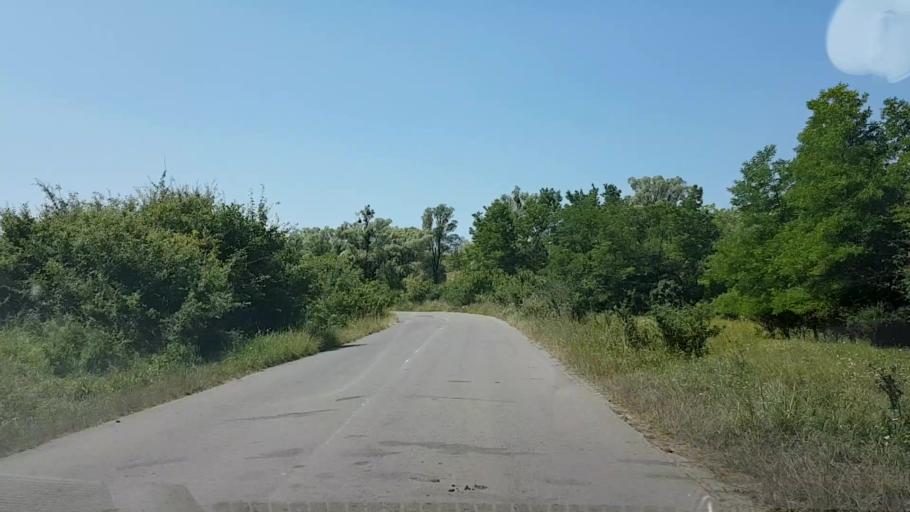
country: RO
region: Brasov
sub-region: Comuna Cincu
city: Cincu
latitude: 45.9497
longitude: 24.7833
